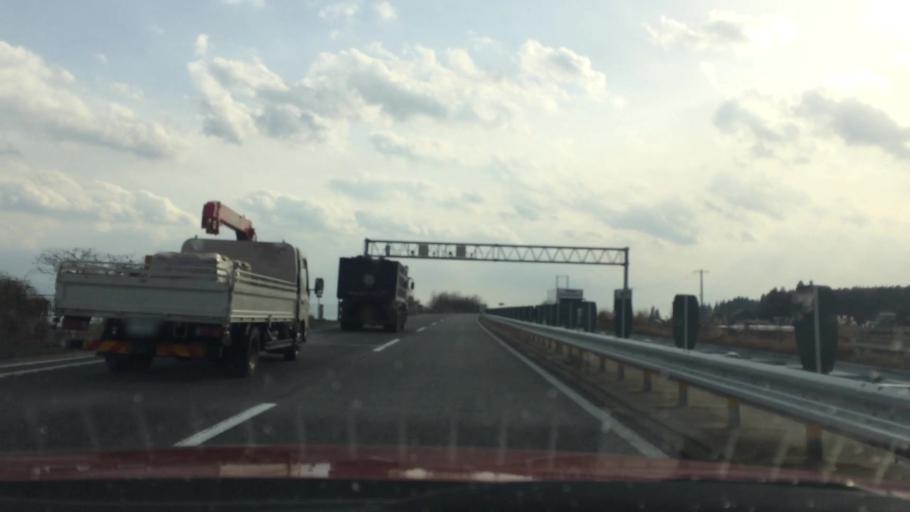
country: JP
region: Nagano
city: Iida
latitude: 35.6653
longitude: 137.9035
